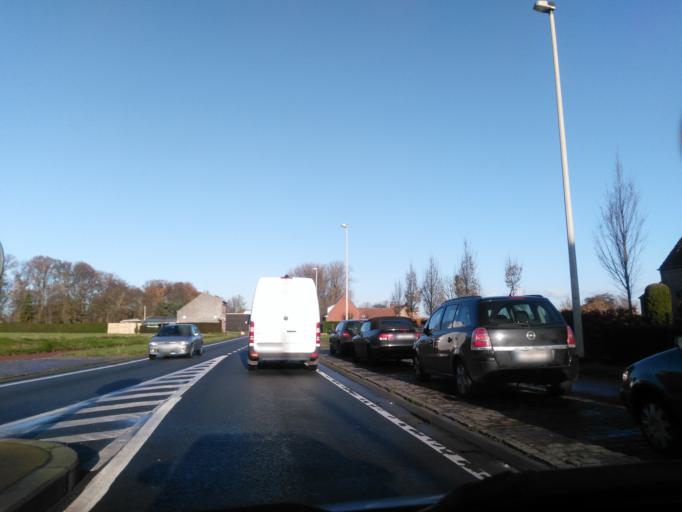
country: BE
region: Flanders
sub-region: Provincie Antwerpen
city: Zwijndrecht
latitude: 51.2075
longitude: 4.3156
